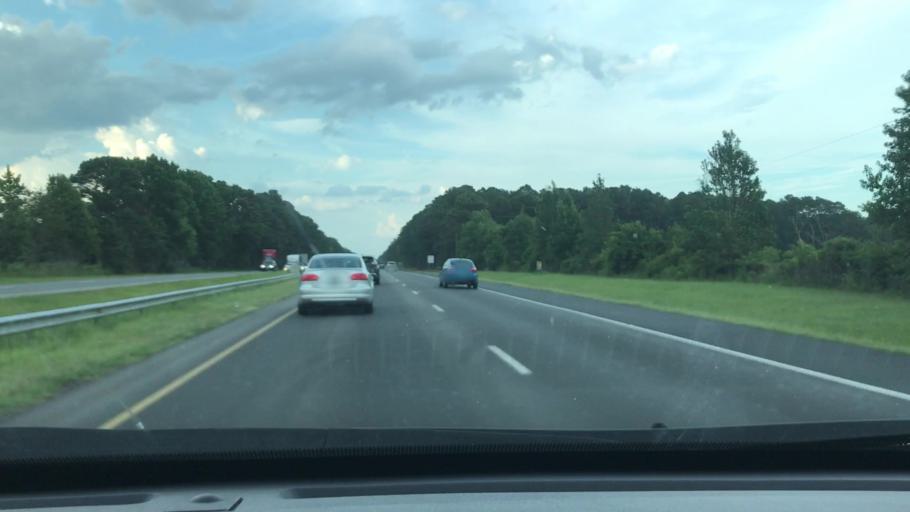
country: US
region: North Carolina
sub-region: Cumberland County
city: Eastover
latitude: 35.1360
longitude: -78.7405
